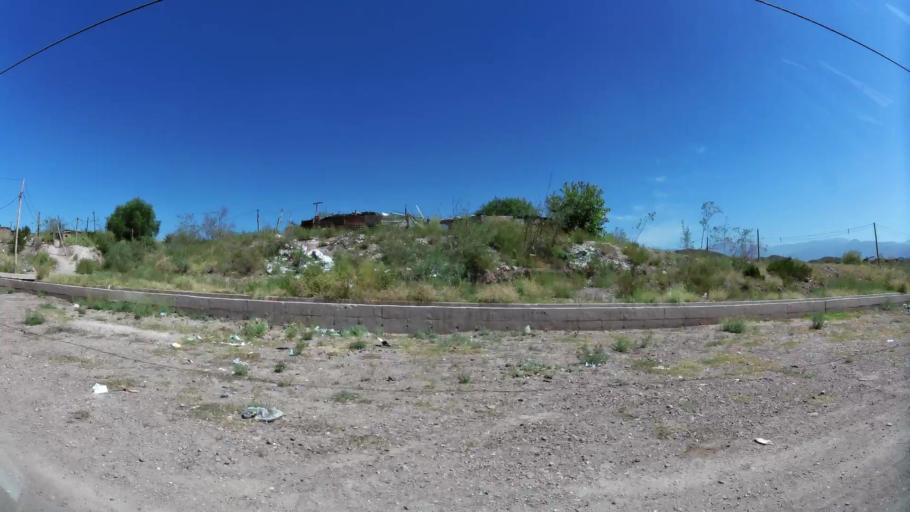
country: AR
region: Mendoza
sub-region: Departamento de Godoy Cruz
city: Godoy Cruz
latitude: -32.9453
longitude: -68.8766
